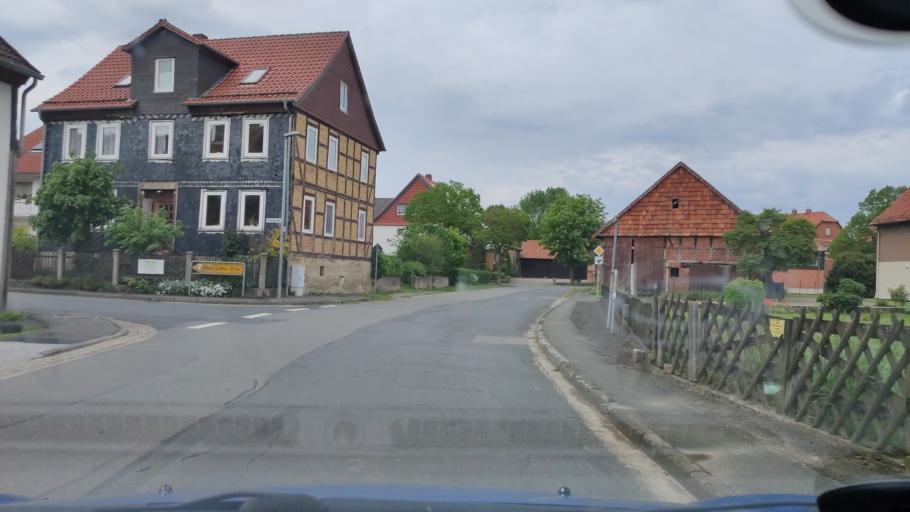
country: DE
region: Lower Saxony
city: Freden
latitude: 51.8887
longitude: 9.8603
